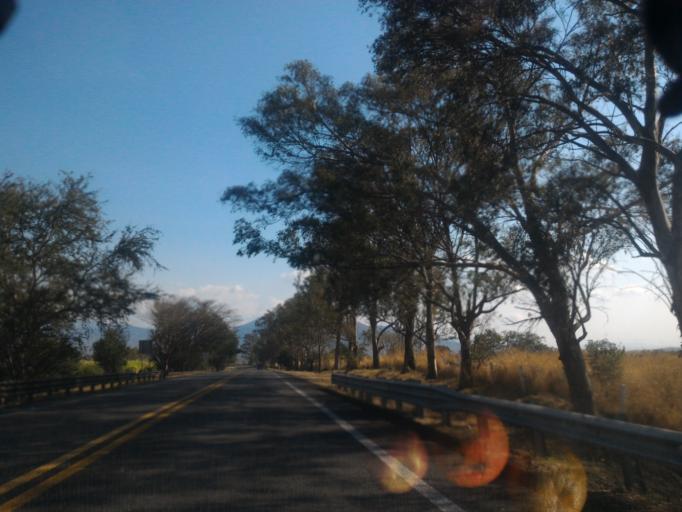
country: MX
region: Jalisco
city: Tuxpan
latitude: 19.5596
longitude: -103.4403
